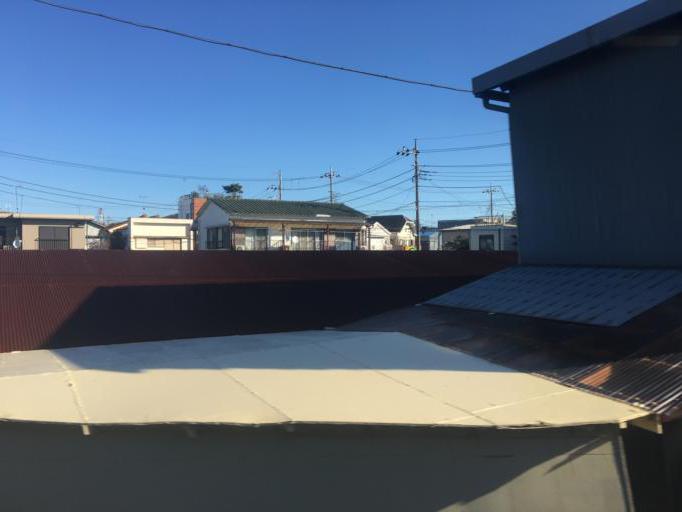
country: JP
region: Chiba
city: Matsudo
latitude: 35.7449
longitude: 139.8799
